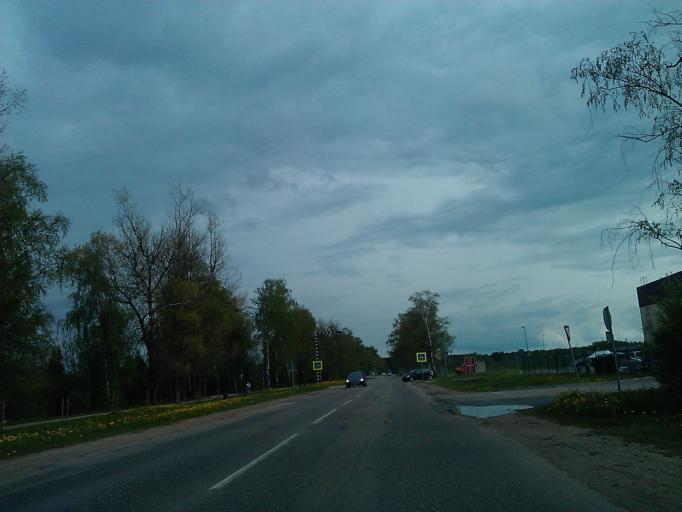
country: LV
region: Adazi
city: Adazi
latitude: 57.0718
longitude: 24.3209
